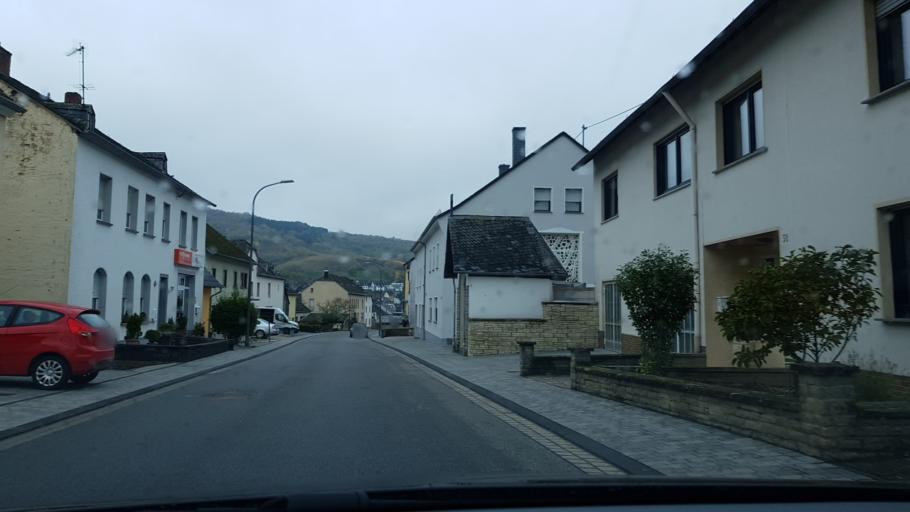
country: DE
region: Rheinland-Pfalz
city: Fell
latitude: 49.7709
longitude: 6.7881
